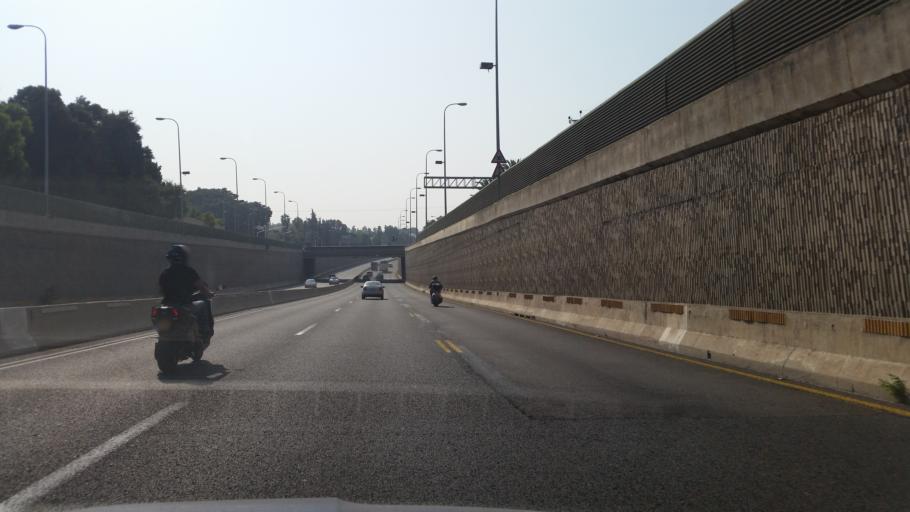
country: IL
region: Tel Aviv
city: Kefar Shemaryahu
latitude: 32.1815
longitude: 34.8156
